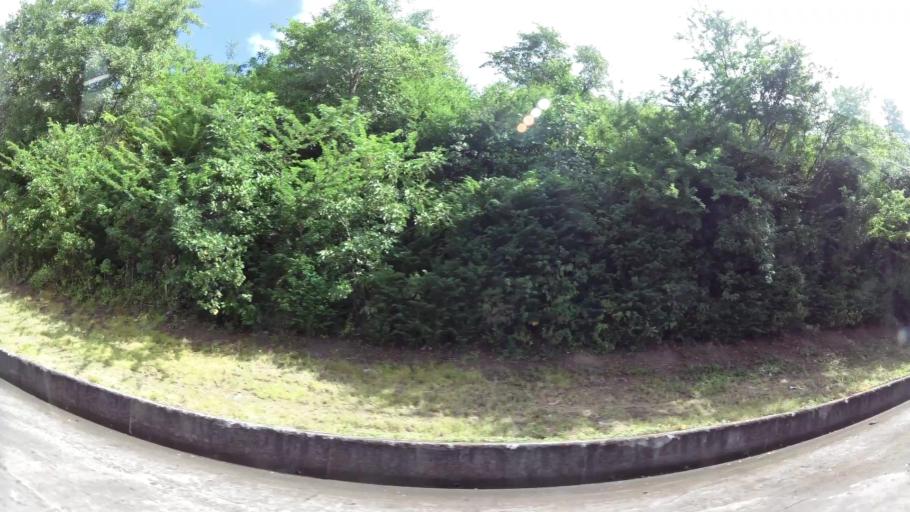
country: MQ
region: Martinique
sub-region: Martinique
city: Fort-de-France
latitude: 14.6017
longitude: -61.0450
